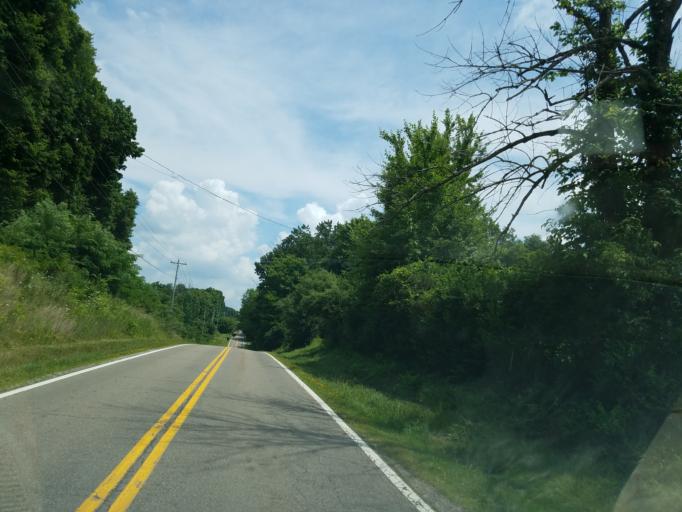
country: US
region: Ohio
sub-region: Licking County
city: Granville
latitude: 40.1537
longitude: -82.5521
